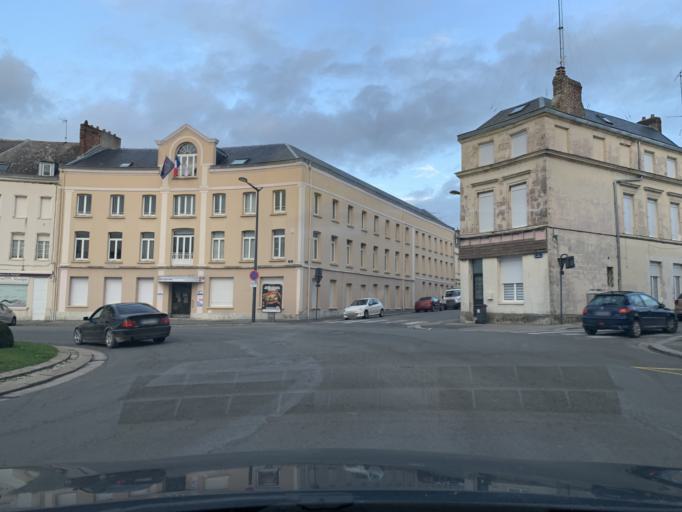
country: FR
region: Picardie
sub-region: Departement de l'Aisne
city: Saint-Quentin
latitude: 49.8510
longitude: 3.2873
